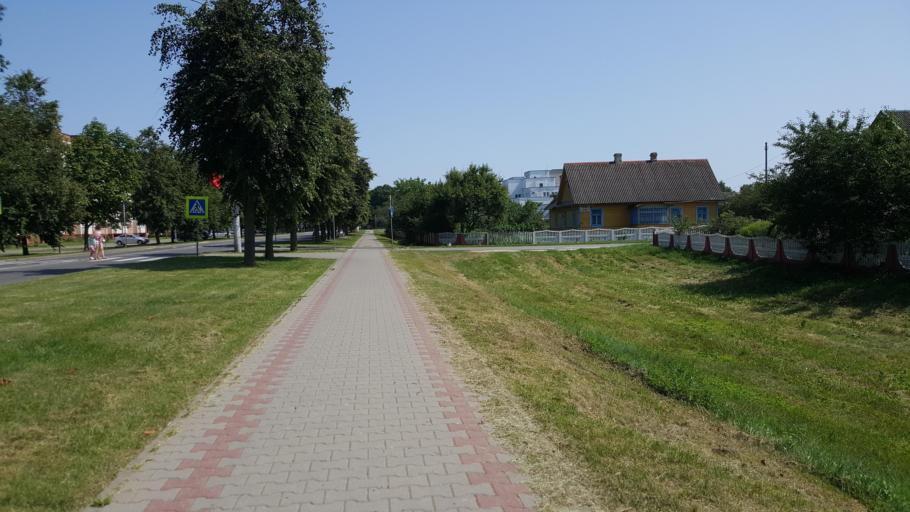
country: BY
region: Brest
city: Zhabinka
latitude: 52.1911
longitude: 24.0265
